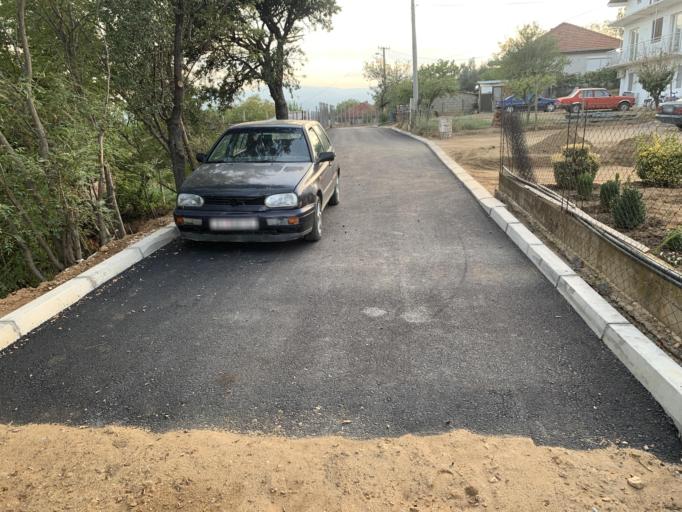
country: MK
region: Bogdanci
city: Bogdanci
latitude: 41.2074
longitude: 22.5804
